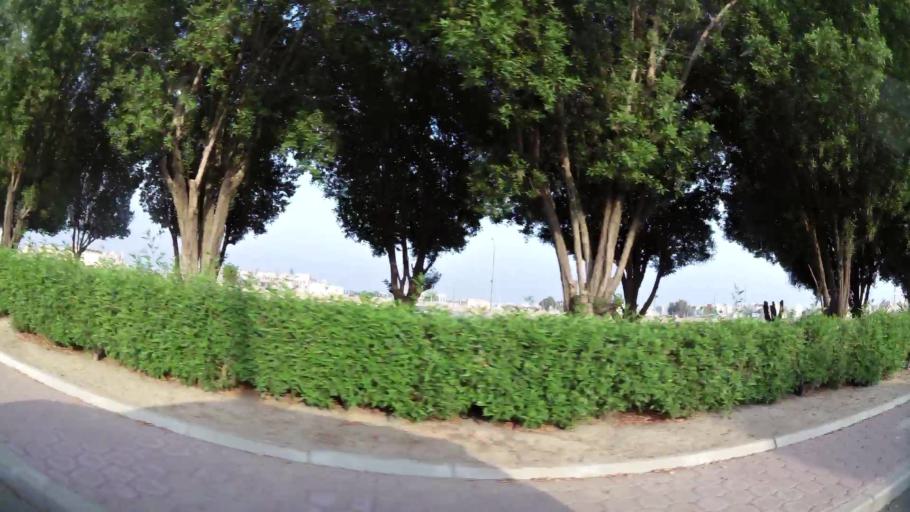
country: KW
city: Al Funaytis
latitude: 29.2400
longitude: 48.0834
